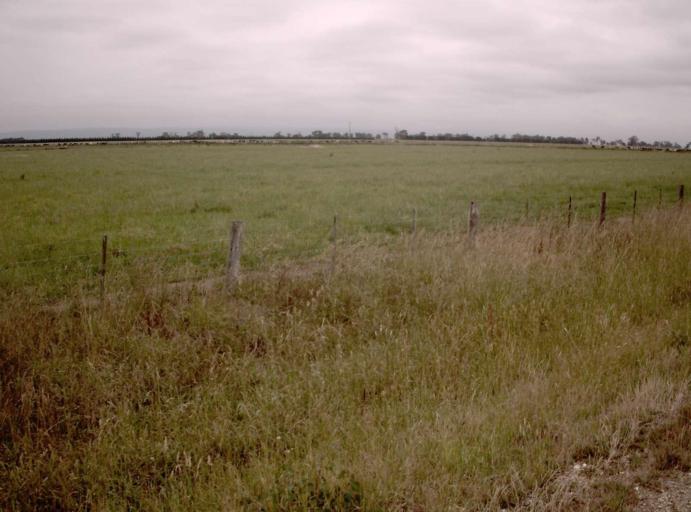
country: AU
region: Victoria
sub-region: Wellington
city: Heyfield
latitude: -38.0745
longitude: 146.7707
